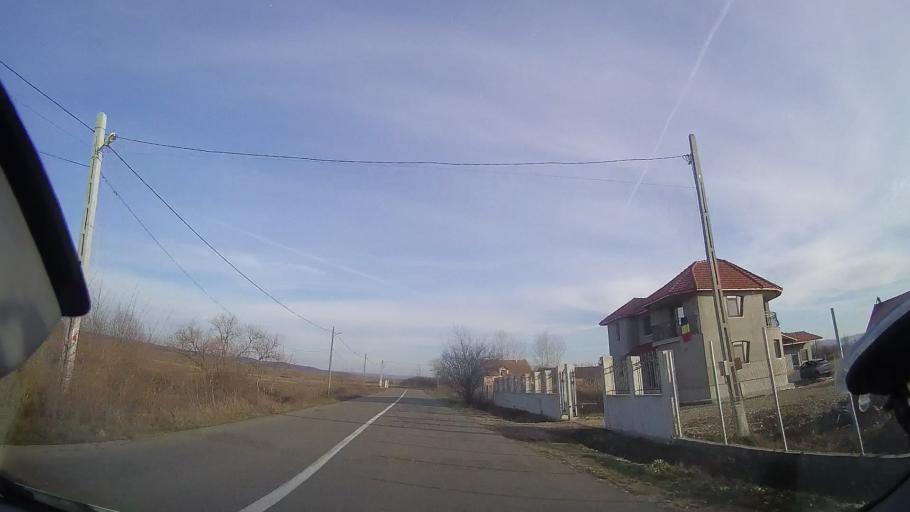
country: RO
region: Bihor
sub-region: Comuna Tileagd
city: Tileagd
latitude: 47.0662
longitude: 22.2136
